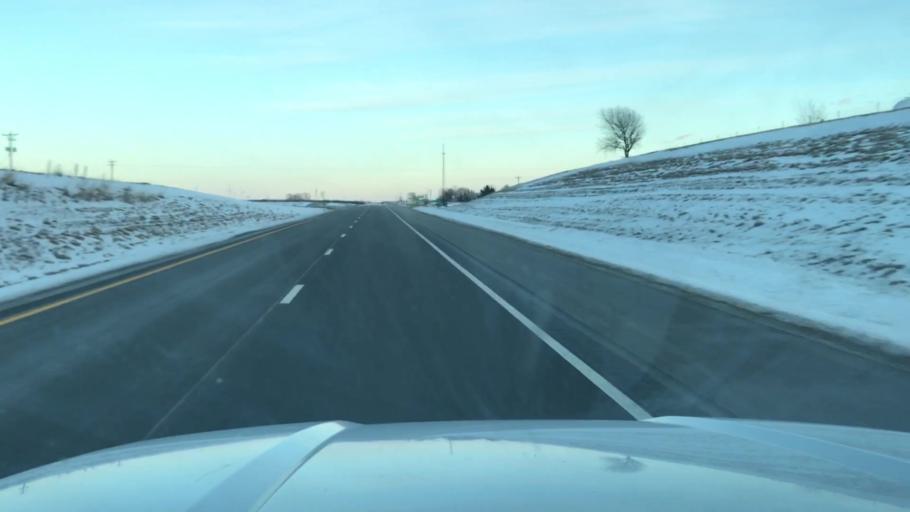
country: US
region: Missouri
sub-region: Clinton County
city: Gower
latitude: 39.7620
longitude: -94.5100
